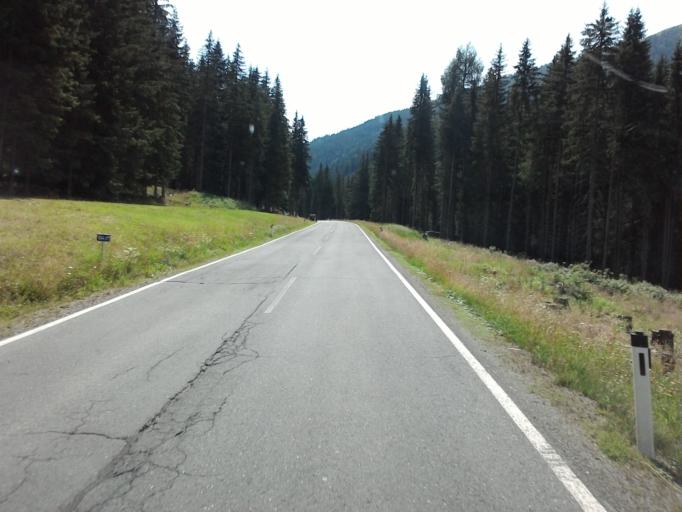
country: AT
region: Tyrol
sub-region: Politischer Bezirk Lienz
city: Obertilliach
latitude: 46.7122
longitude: 12.5788
